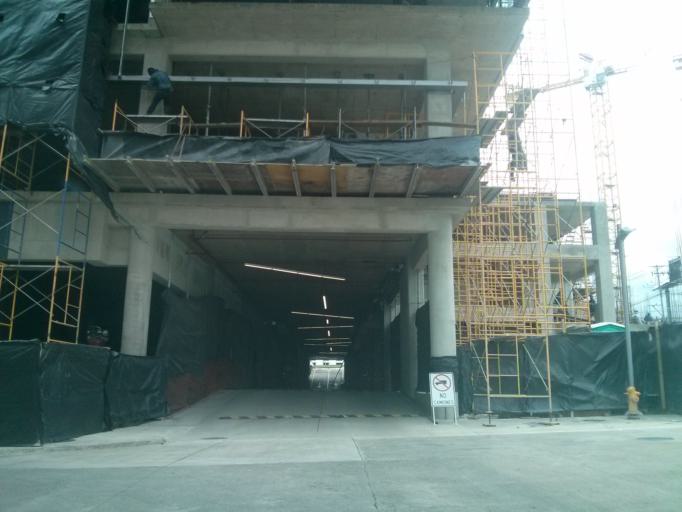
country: CR
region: San Jose
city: San Rafael
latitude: 9.9383
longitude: -84.1422
